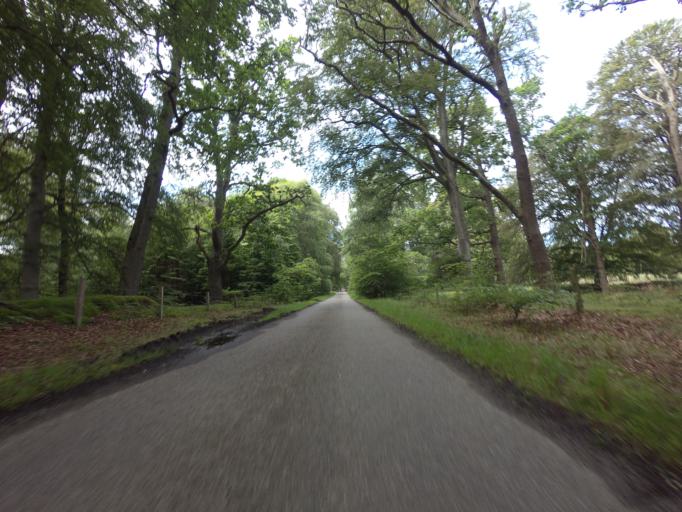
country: GB
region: Scotland
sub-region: Moray
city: Hopeman
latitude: 57.6708
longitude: -3.4140
